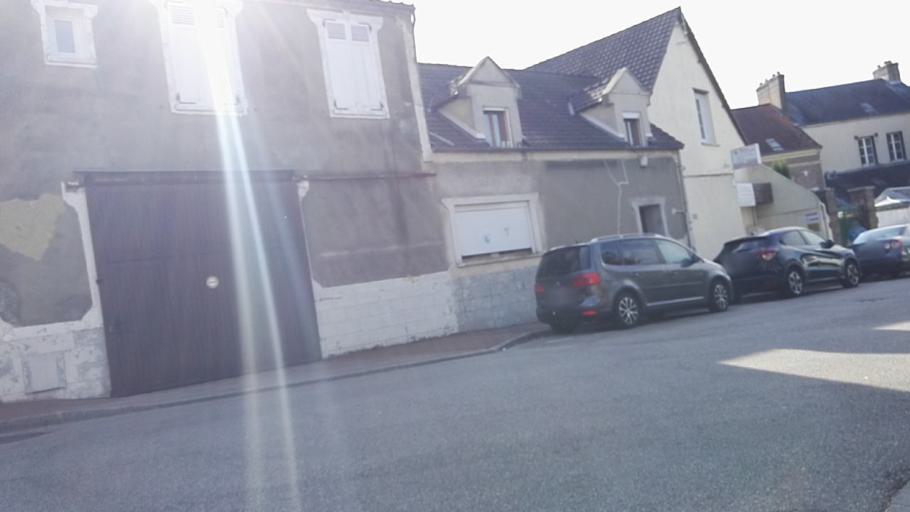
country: FR
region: Haute-Normandie
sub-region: Departement de l'Eure
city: Pacy-sur-Eure
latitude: 49.0151
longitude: 1.3819
